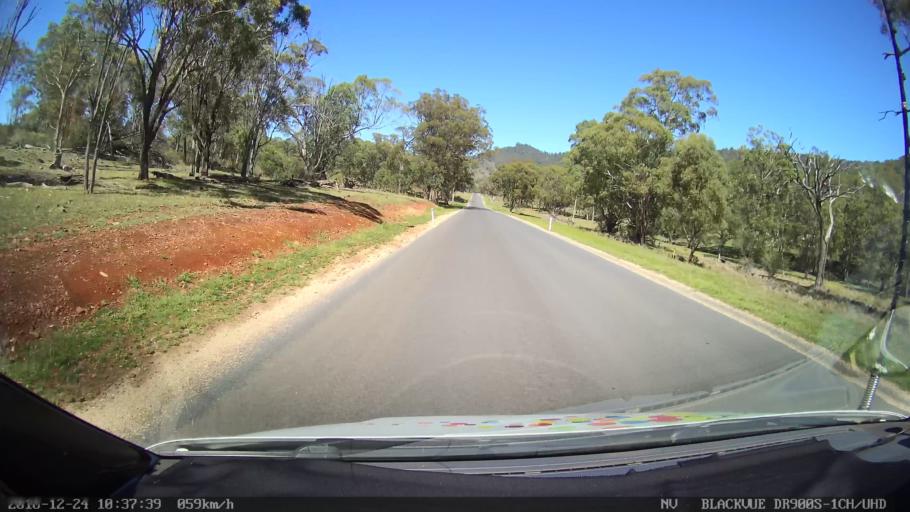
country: AU
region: New South Wales
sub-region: Upper Hunter Shire
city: Merriwa
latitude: -31.8465
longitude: 150.4911
